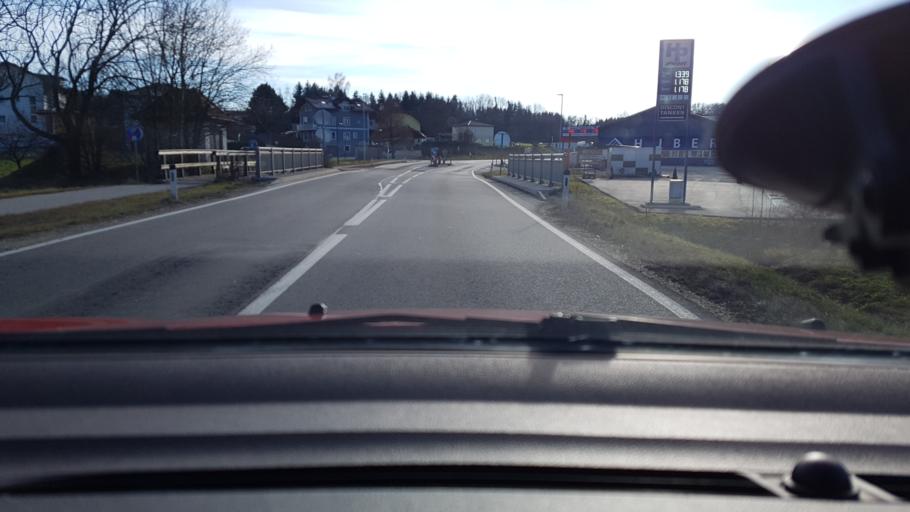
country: AT
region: Salzburg
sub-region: Politischer Bezirk Salzburg-Umgebung
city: Dorfbeuern
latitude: 48.0386
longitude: 12.9882
